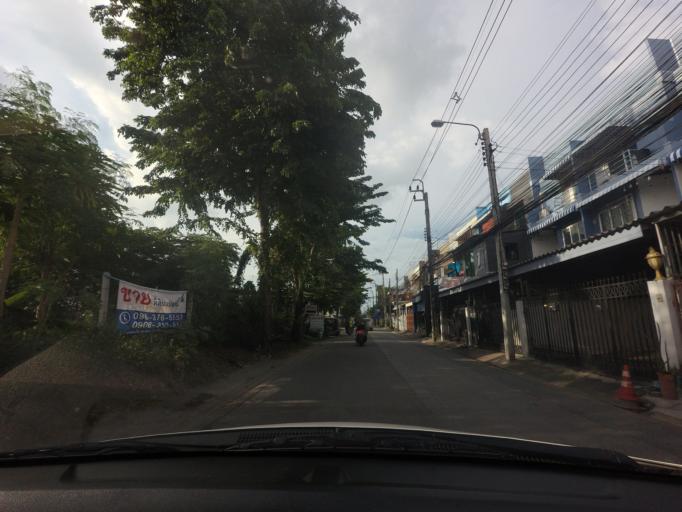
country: TH
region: Bangkok
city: Lak Si
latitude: 13.8936
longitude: 100.5782
